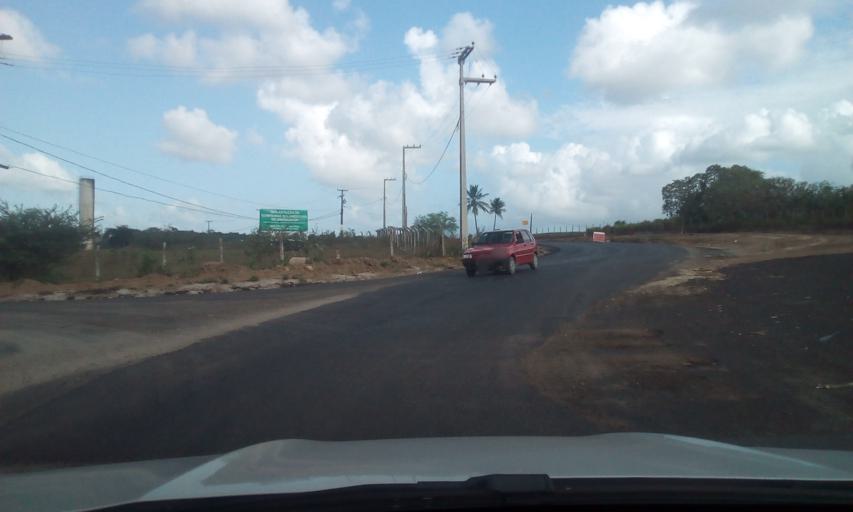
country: BR
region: Paraiba
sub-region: Conde
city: Conde
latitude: -7.1942
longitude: -34.8984
